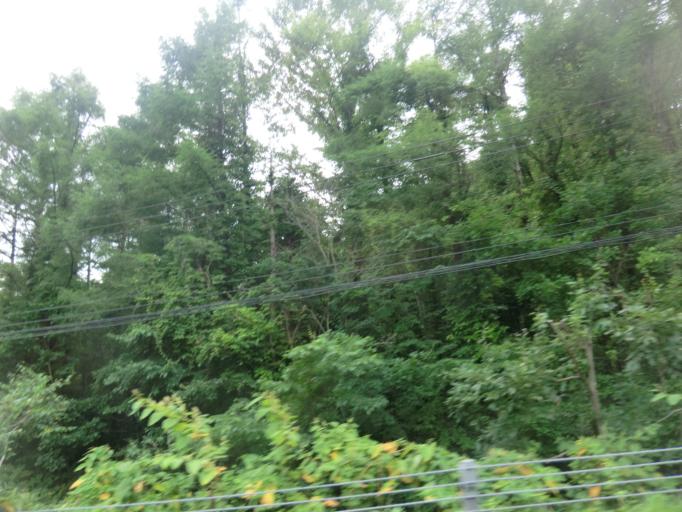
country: JP
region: Hokkaido
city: Date
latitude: 42.5452
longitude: 140.8571
